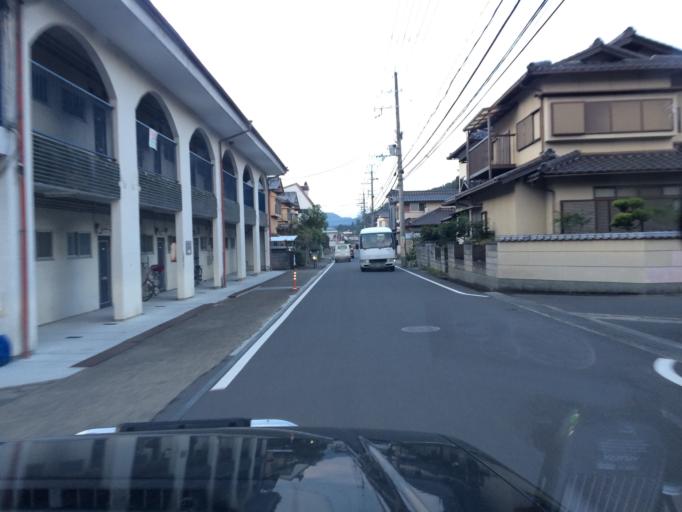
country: JP
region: Kyoto
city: Kameoka
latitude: 35.0964
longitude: 135.4748
